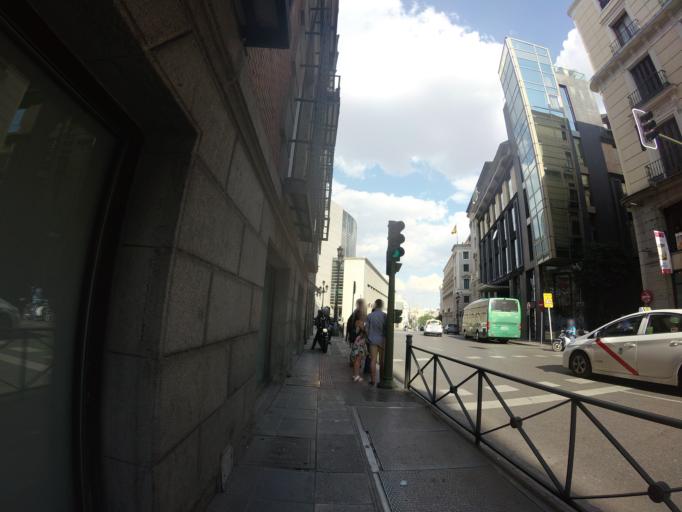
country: ES
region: Madrid
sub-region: Provincia de Madrid
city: Madrid
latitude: 40.4166
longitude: -3.6990
